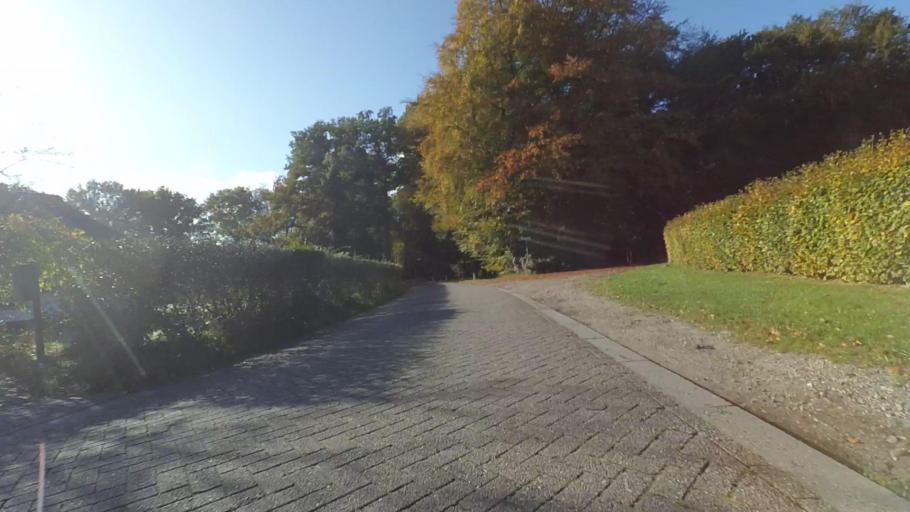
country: NL
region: Gelderland
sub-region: Gemeente Barneveld
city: Zwartebroek
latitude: 52.2051
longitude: 5.5152
